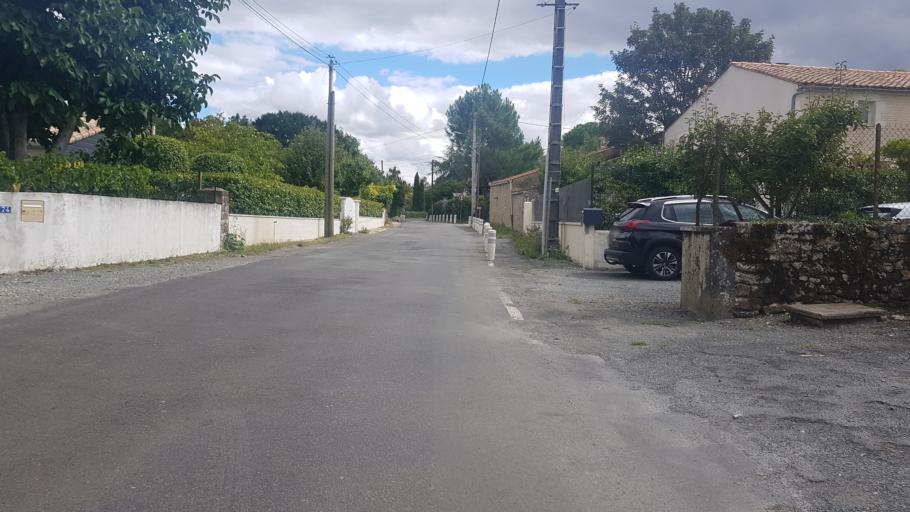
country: FR
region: Poitou-Charentes
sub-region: Departement des Deux-Sevres
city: Vouille
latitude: 46.3281
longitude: -0.3451
